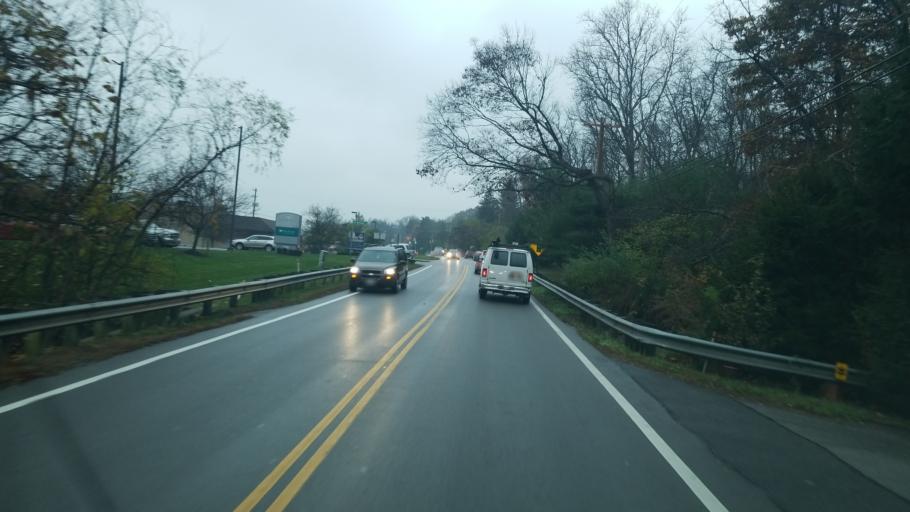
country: US
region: Ohio
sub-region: Franklin County
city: Worthington
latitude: 40.1275
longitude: -83.0366
